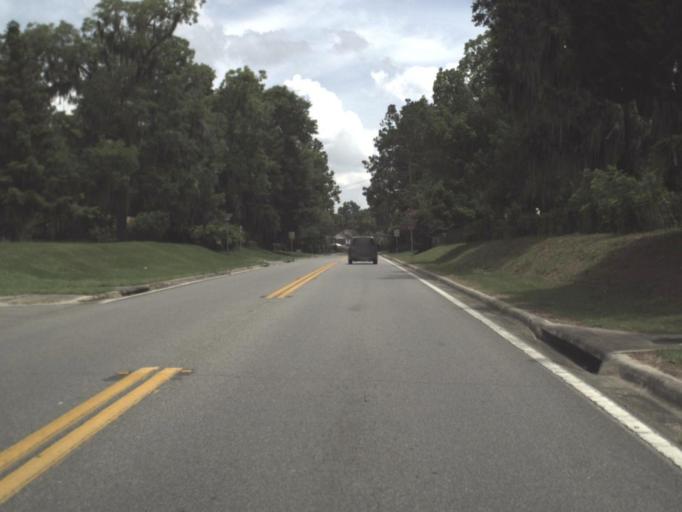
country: US
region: Florida
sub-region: Madison County
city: Madison
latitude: 30.4747
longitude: -83.4155
